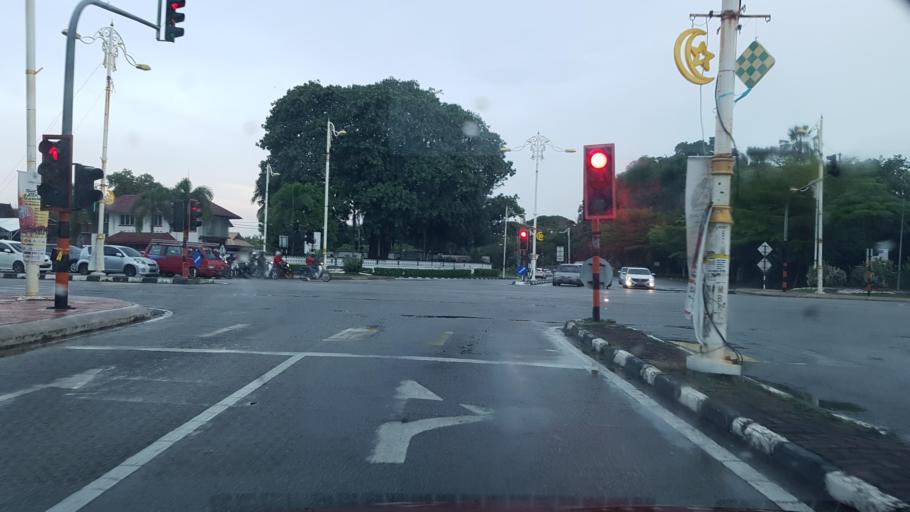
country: MY
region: Terengganu
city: Kuala Terengganu
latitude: 5.3191
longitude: 103.1537
